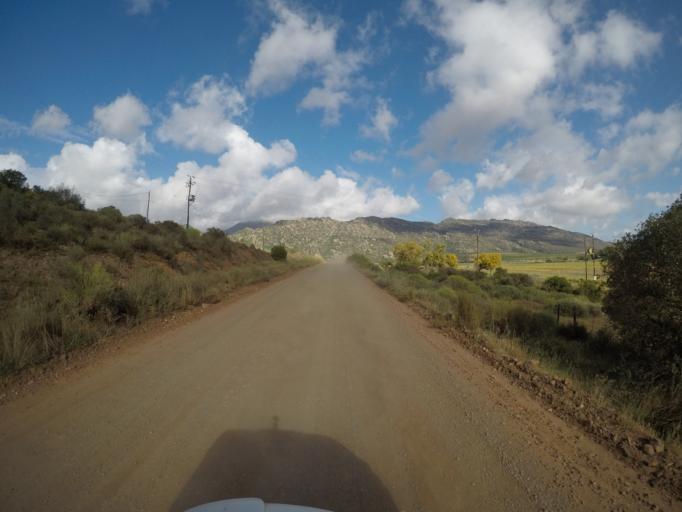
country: ZA
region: Western Cape
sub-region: West Coast District Municipality
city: Clanwilliam
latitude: -32.3634
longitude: 18.9439
